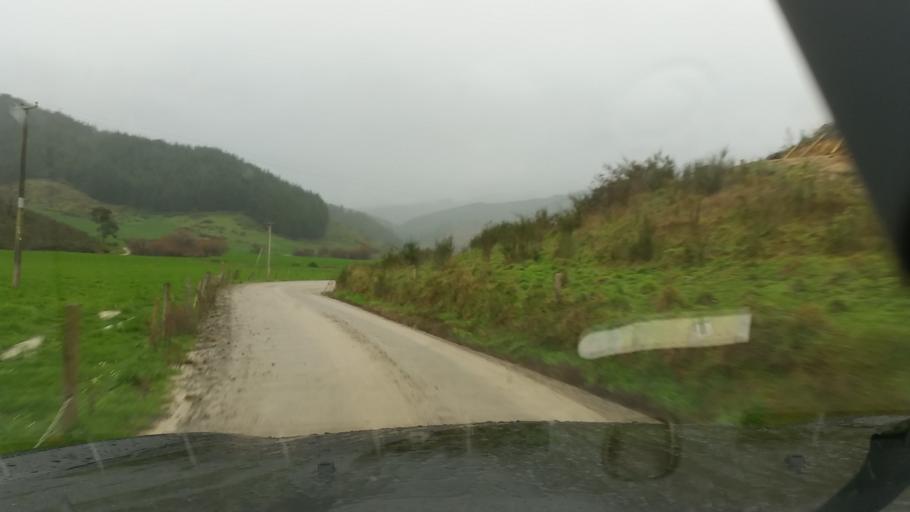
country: NZ
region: Marlborough
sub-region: Marlborough District
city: Picton
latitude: -41.3305
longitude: 173.9345
